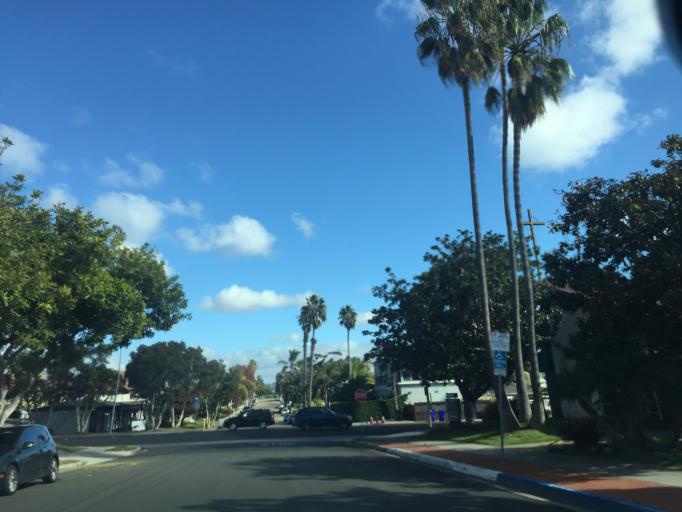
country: US
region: California
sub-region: San Diego County
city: La Jolla
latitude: 32.7968
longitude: -117.2405
